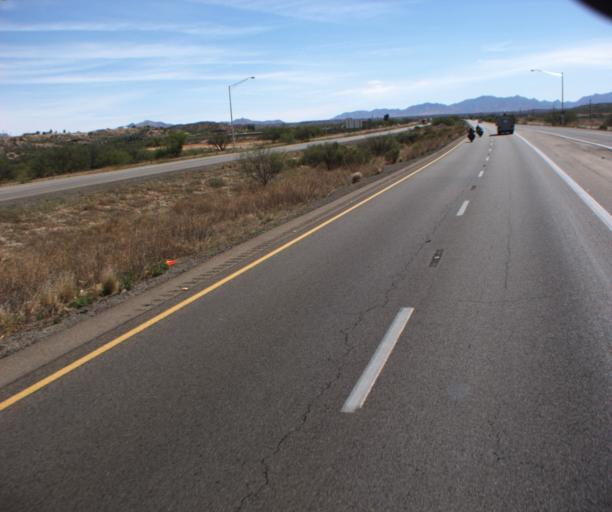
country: US
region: Arizona
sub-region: Cochise County
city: Benson
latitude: 31.9653
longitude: -110.2677
